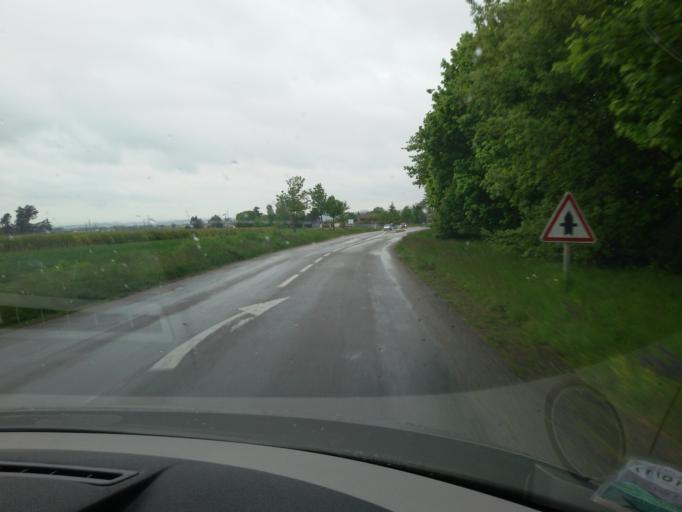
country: FR
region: Rhone-Alpes
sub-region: Departement de la Drome
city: Chatuzange-le-Goubet
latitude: 45.0148
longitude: 5.0829
